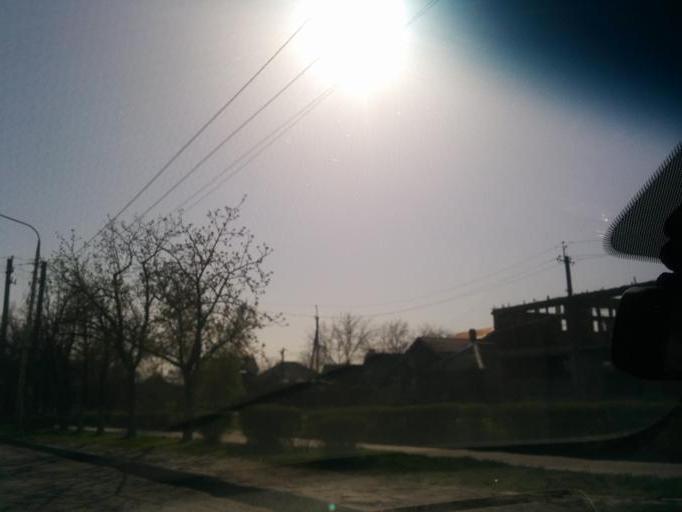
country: RU
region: Rostov
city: Shakhty
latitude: 47.6980
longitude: 40.2080
